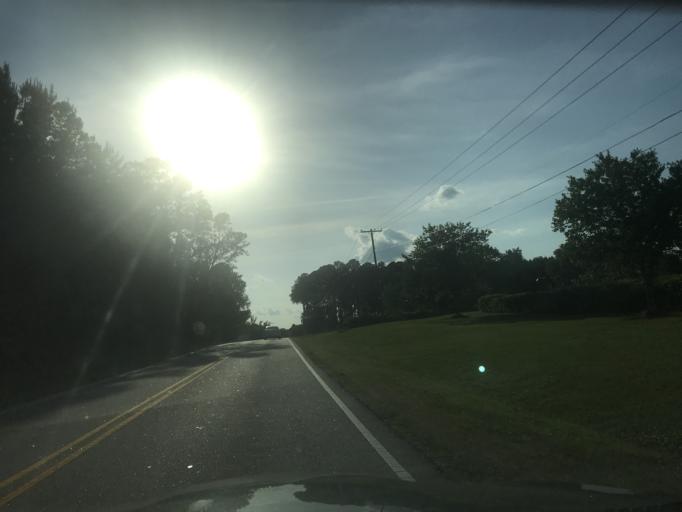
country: US
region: North Carolina
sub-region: Wake County
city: Knightdale
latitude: 35.7523
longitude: -78.4964
